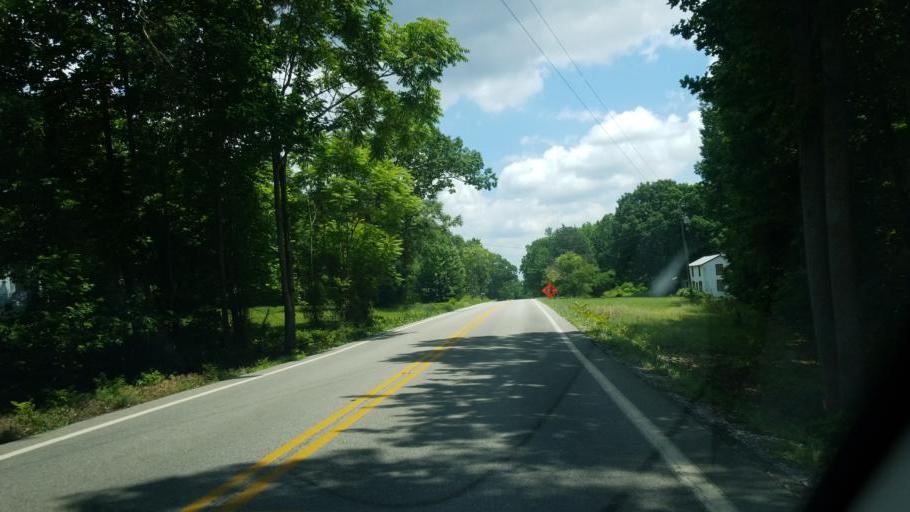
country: US
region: Virginia
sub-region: Buckingham County
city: Buckingham
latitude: 37.5303
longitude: -78.7207
